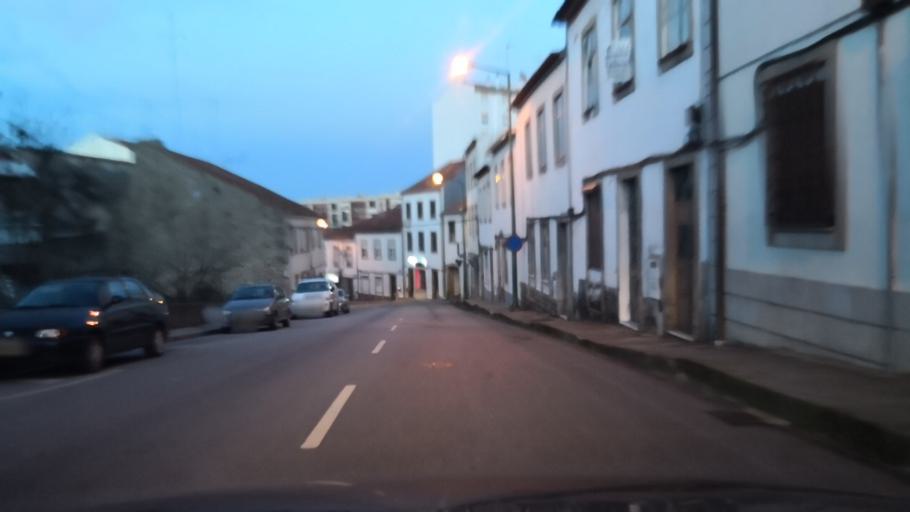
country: PT
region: Castelo Branco
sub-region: Castelo Branco
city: Castelo Branco
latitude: 39.8245
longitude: -7.4863
